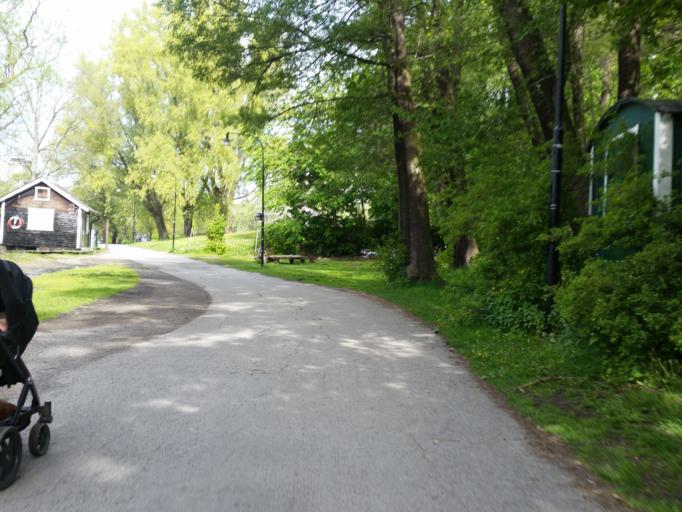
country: SE
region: Stockholm
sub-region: Stockholms Kommun
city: Arsta
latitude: 59.3085
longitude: 18.0509
